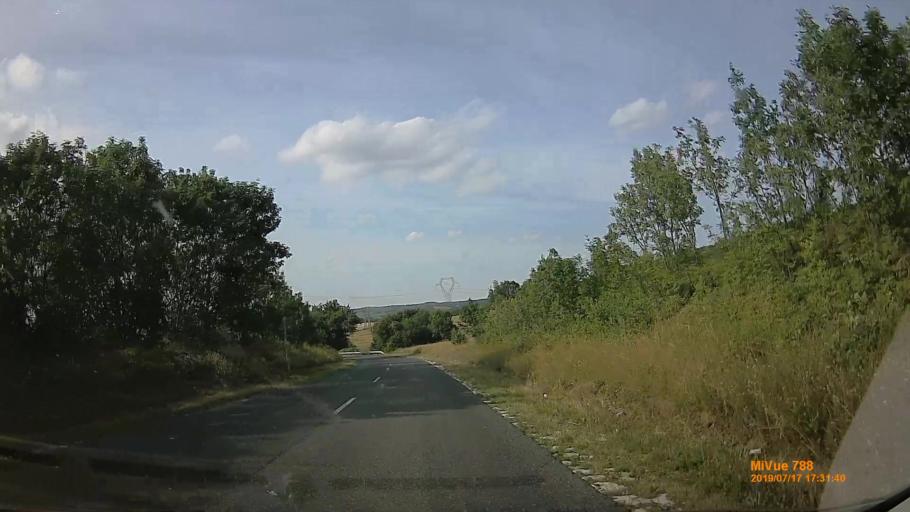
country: HU
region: Veszprem
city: Ajka
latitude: 47.0324
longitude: 17.5576
